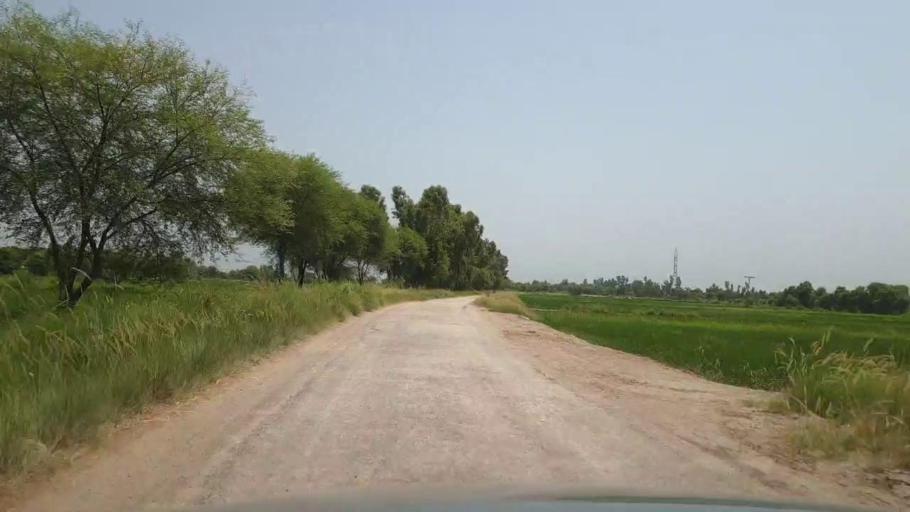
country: PK
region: Sindh
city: Ratodero
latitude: 27.7997
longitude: 68.3441
